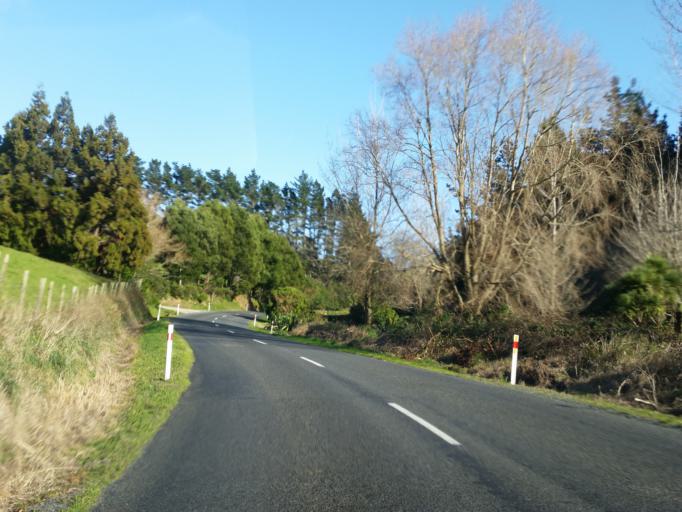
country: NZ
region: Waikato
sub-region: Hauraki District
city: Waihi
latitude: -37.4361
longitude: 175.7786
